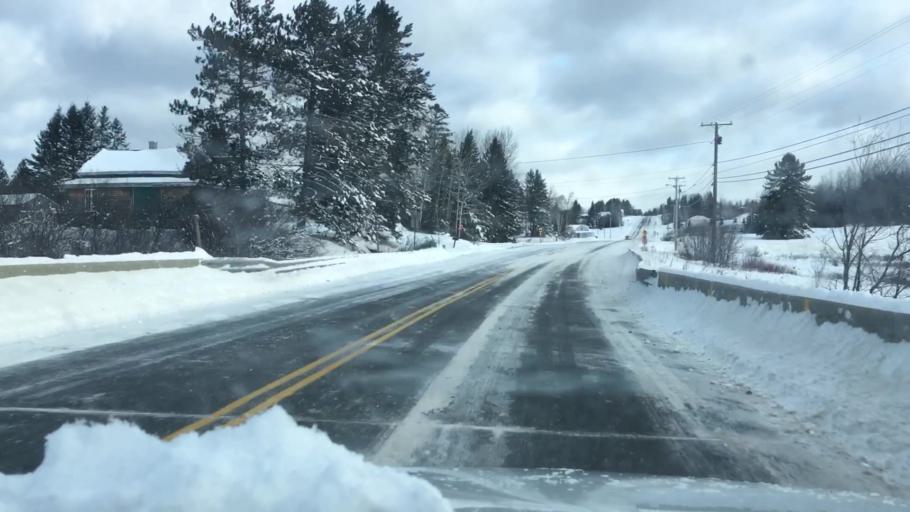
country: US
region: Maine
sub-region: Aroostook County
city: Caribou
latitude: 46.9785
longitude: -68.0353
